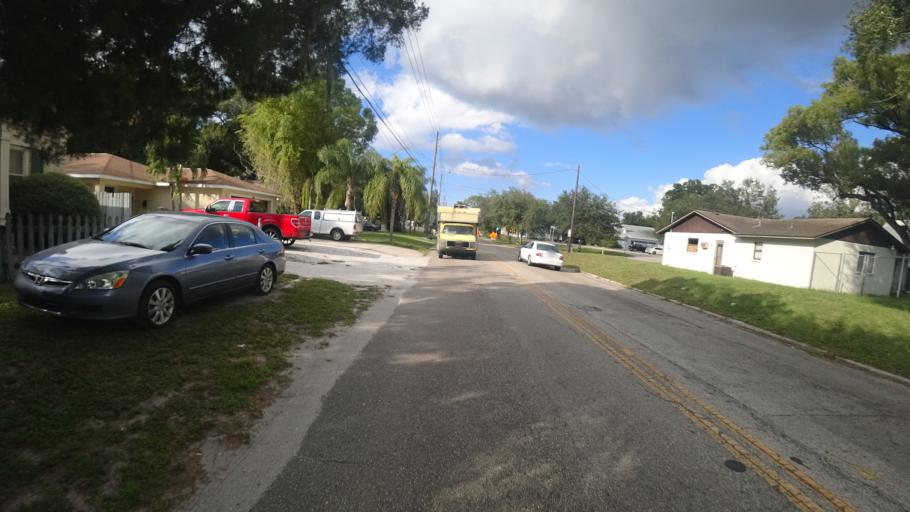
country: US
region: Florida
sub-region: Manatee County
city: Bradenton
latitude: 27.4904
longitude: -82.5876
